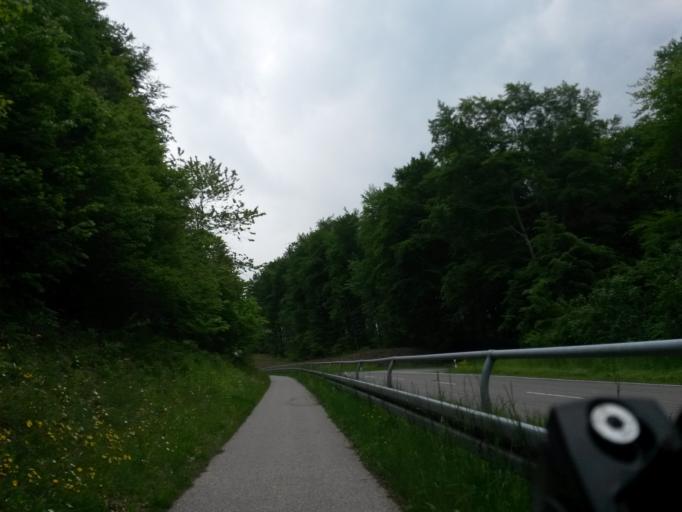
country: DE
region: Baden-Wuerttemberg
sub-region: Tuebingen Region
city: Bad Waldsee
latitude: 47.9229
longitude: 9.7797
